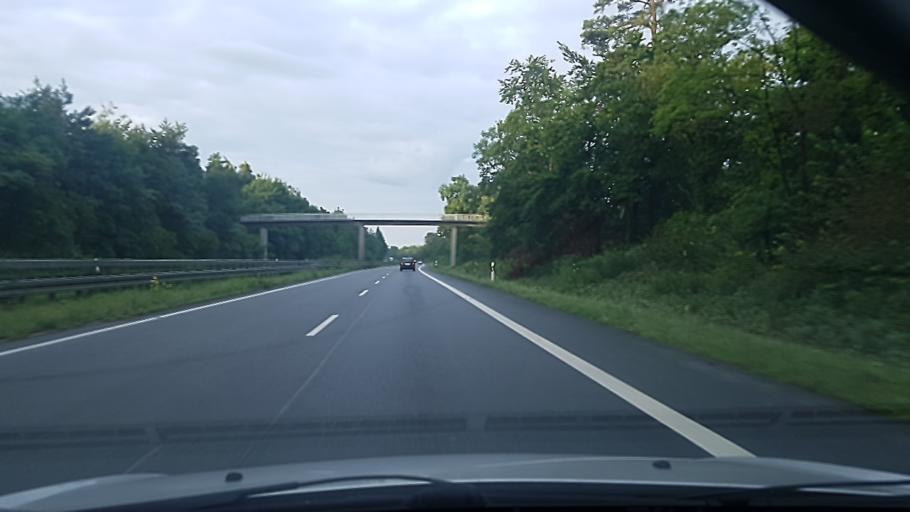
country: DE
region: Hesse
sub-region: Regierungsbezirk Darmstadt
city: Darmstadt
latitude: 49.8413
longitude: 8.6379
